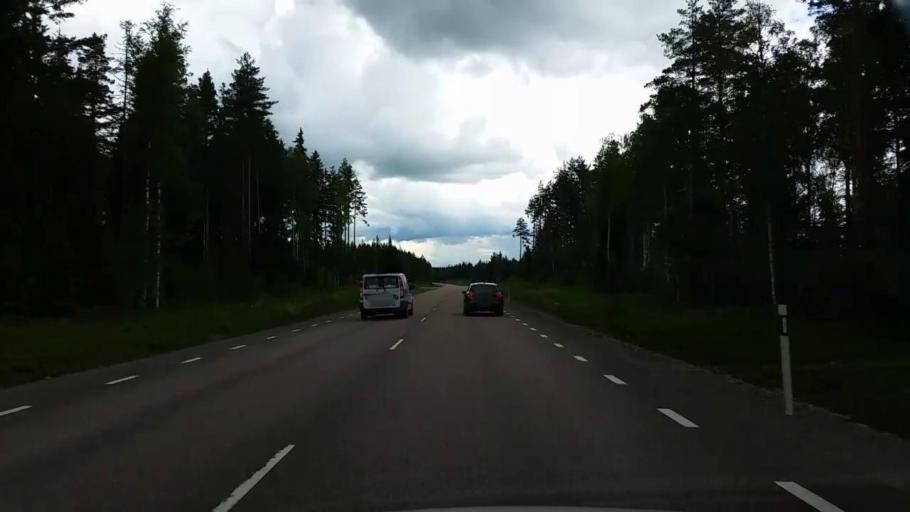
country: SE
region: Dalarna
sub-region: Avesta Kommun
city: Horndal
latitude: 60.4623
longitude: 16.4470
